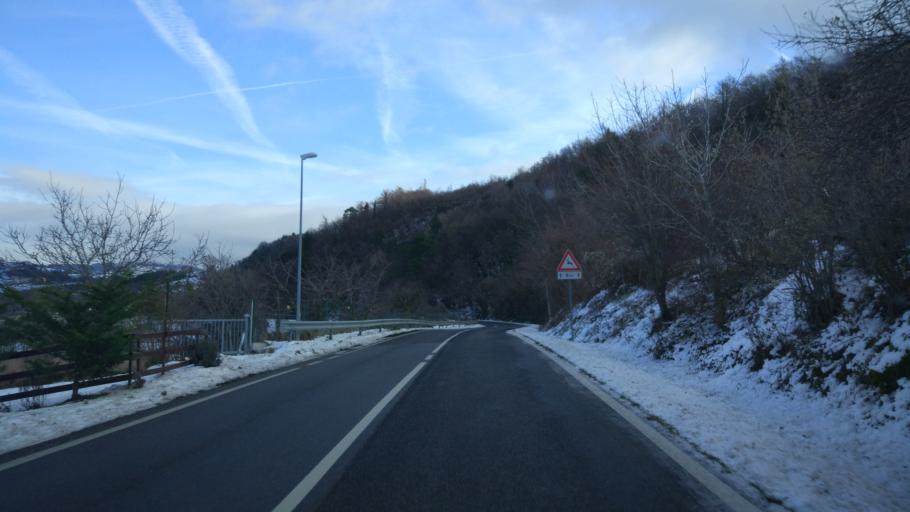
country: IT
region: Veneto
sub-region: Provincia di Verona
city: Sant'Anna d'Alfaedo
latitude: 45.6085
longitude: 10.9363
